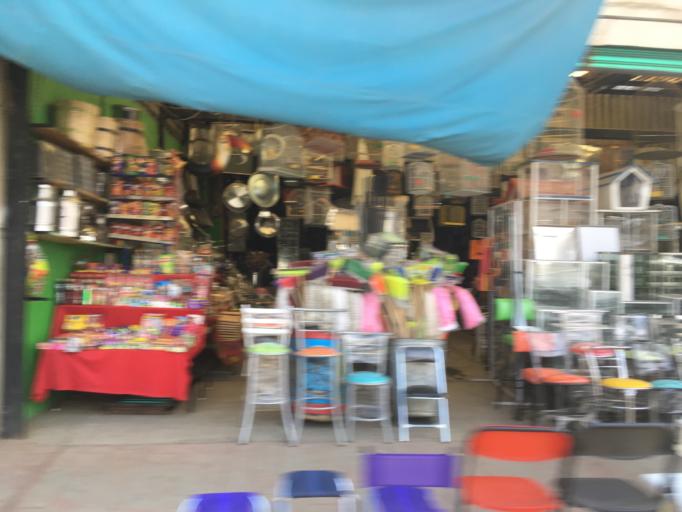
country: MX
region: Mexico
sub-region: Atlacomulco
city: Santiago Acutzilapan
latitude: 19.7916
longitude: -99.7647
